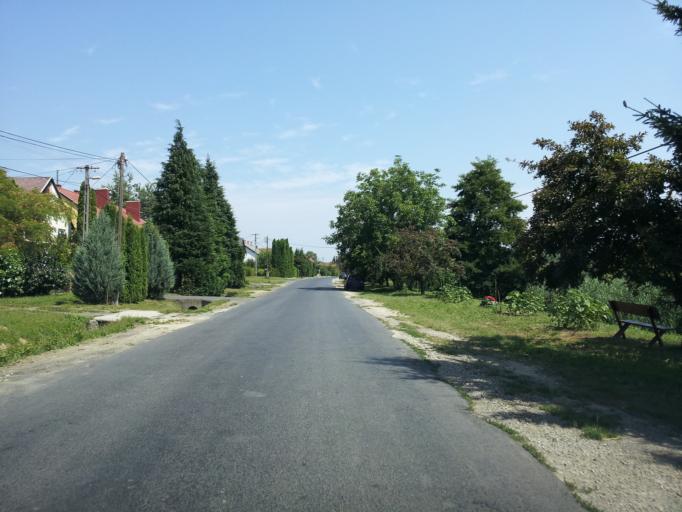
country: HU
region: Zala
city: Pacsa
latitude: 46.8091
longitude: 16.9844
